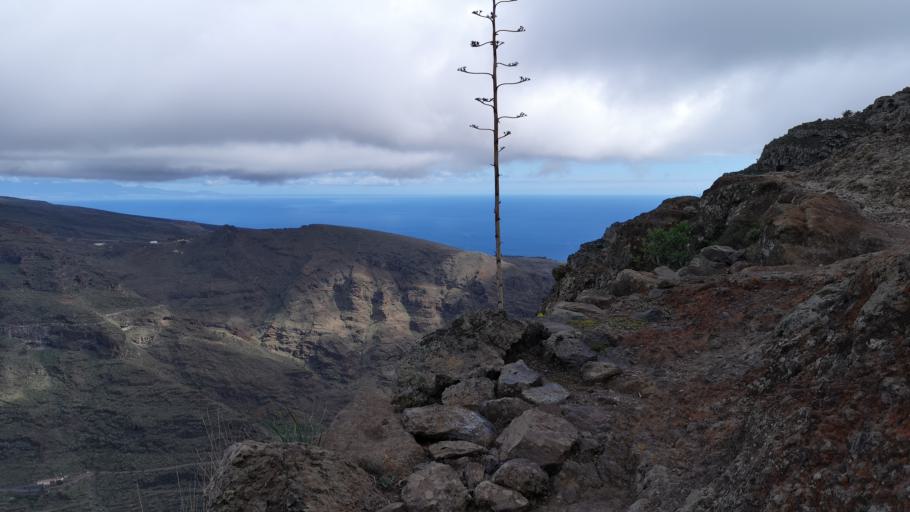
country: ES
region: Canary Islands
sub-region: Provincia de Santa Cruz de Tenerife
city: Alajero
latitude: 28.0609
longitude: -17.2253
